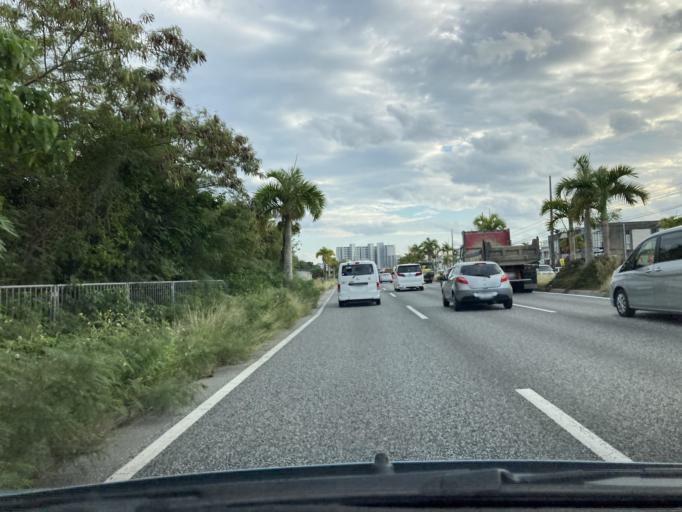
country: JP
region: Okinawa
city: Chatan
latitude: 26.3333
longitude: 127.7517
